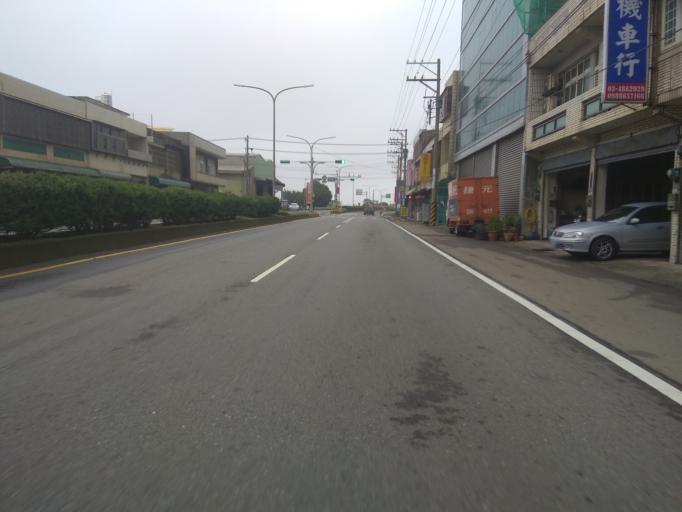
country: TW
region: Taiwan
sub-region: Hsinchu
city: Zhubei
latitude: 25.0083
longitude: 121.0446
